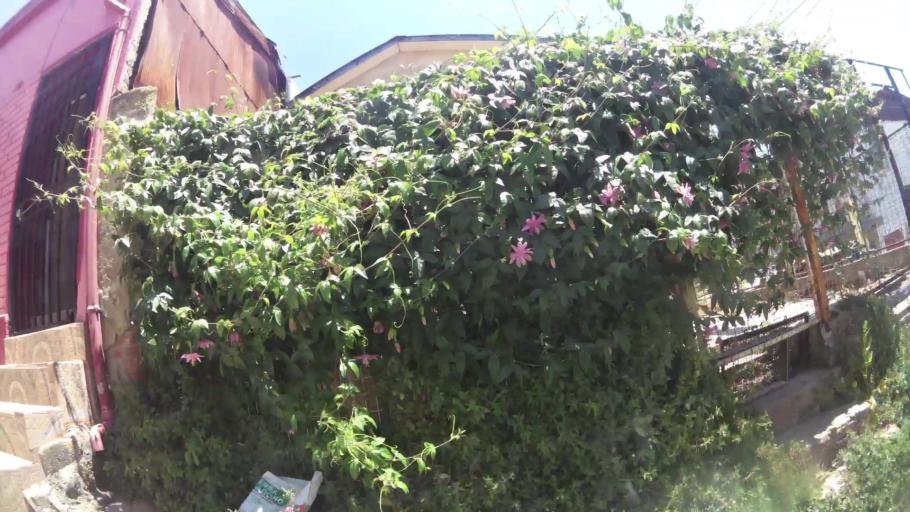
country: CL
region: Valparaiso
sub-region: Provincia de Valparaiso
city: Valparaiso
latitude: -33.0399
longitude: -71.6338
